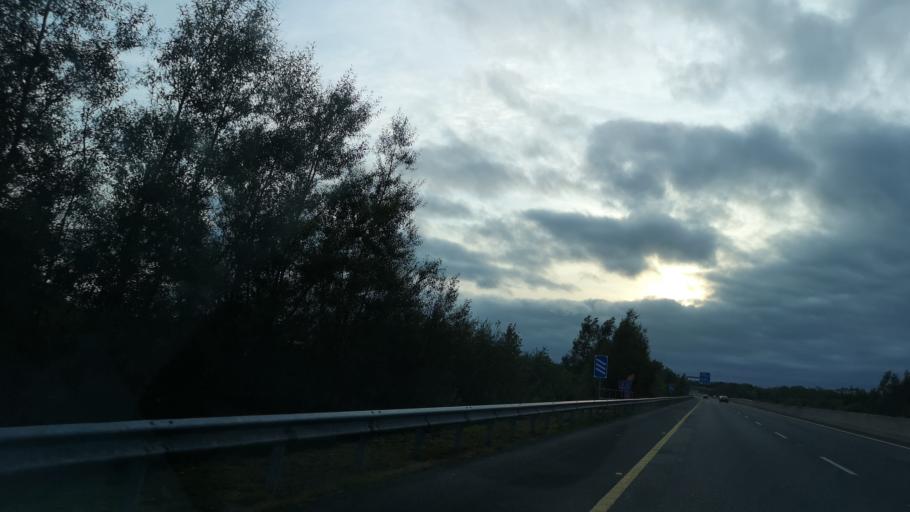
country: IE
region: Connaught
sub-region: County Galway
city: Ballinasloe
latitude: 53.3173
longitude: -8.2271
